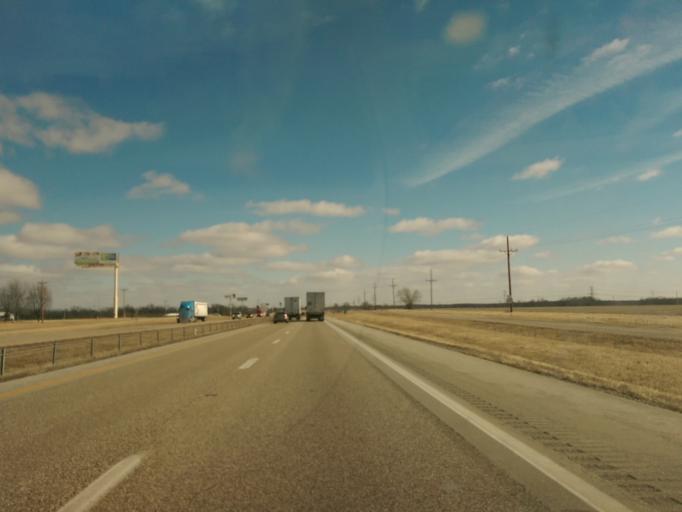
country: US
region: Missouri
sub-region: Montgomery County
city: Montgomery City
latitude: 38.9053
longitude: -91.5039
